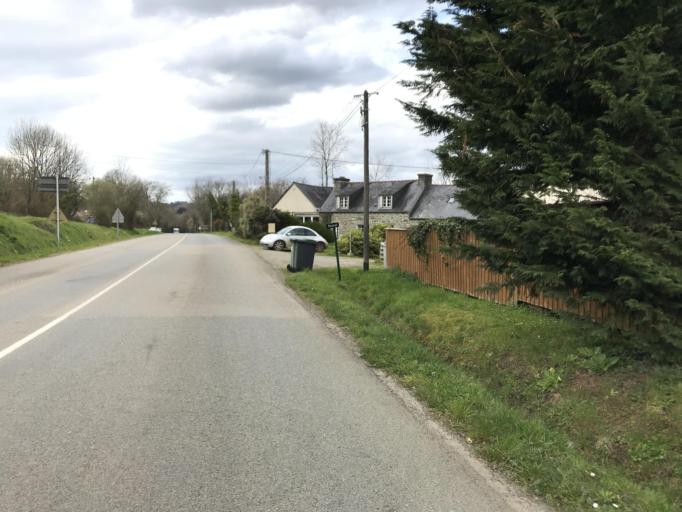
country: FR
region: Brittany
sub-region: Departement du Finistere
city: Le Faou
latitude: 48.3126
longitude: -4.2094
